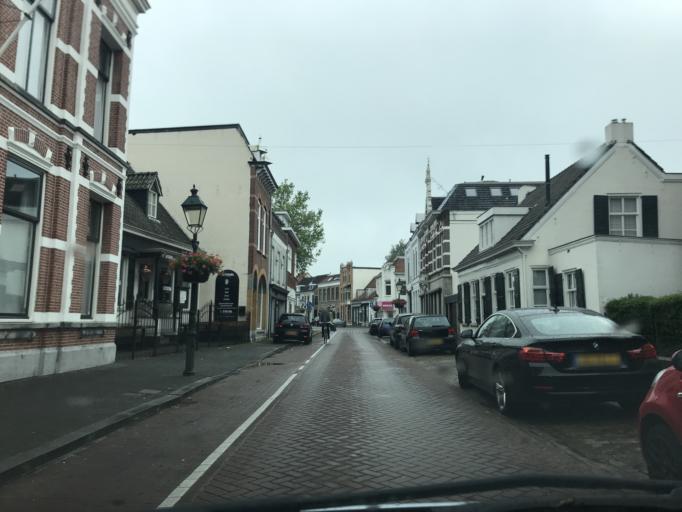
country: NL
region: North Brabant
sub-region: Gemeente Breda
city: Breda
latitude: 51.5696
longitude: 4.7844
